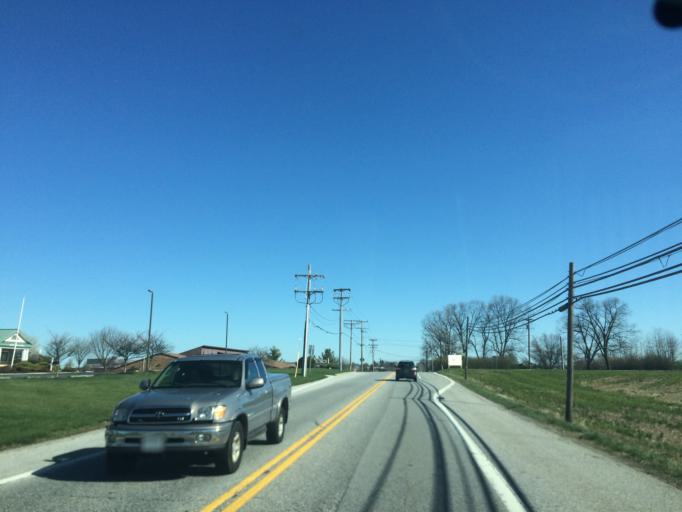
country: US
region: Maryland
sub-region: Carroll County
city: Westminster
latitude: 39.6009
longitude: -76.9988
